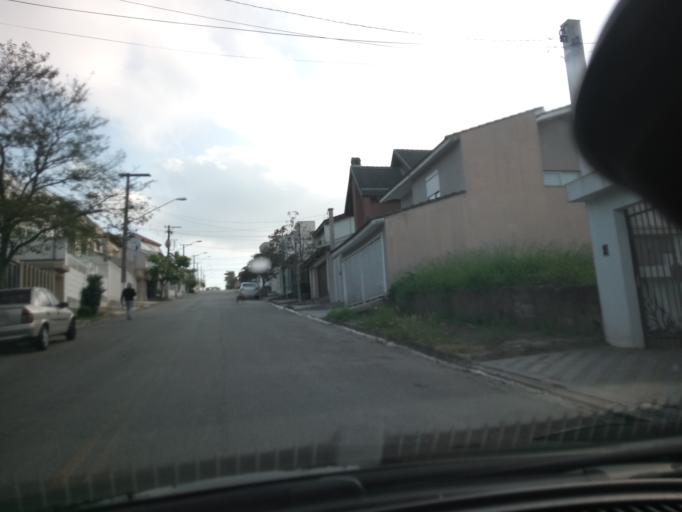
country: BR
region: Sao Paulo
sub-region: Sao Bernardo Do Campo
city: Sao Bernardo do Campo
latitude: -23.7080
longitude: -46.5774
